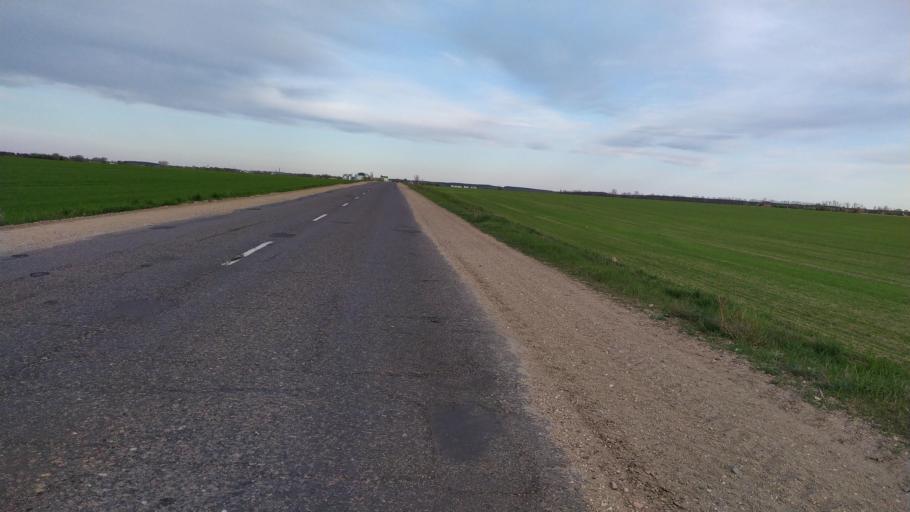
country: BY
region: Brest
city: Kamyanyets
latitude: 52.4053
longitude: 23.7526
